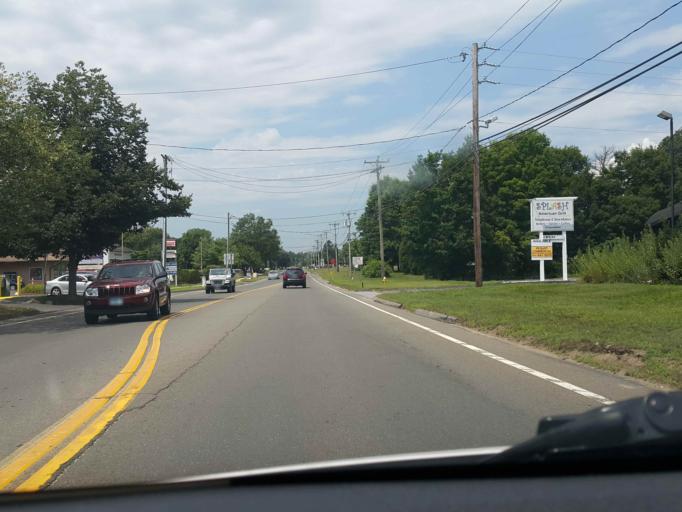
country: US
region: Connecticut
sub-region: New Haven County
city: Guilford Center
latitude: 41.2887
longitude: -72.6652
